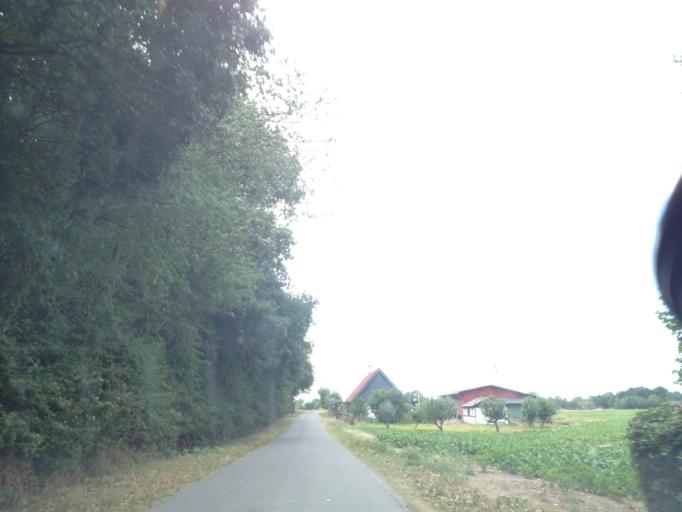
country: DK
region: Zealand
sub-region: Guldborgsund Kommune
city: Sakskobing
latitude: 54.7519
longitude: 11.6738
